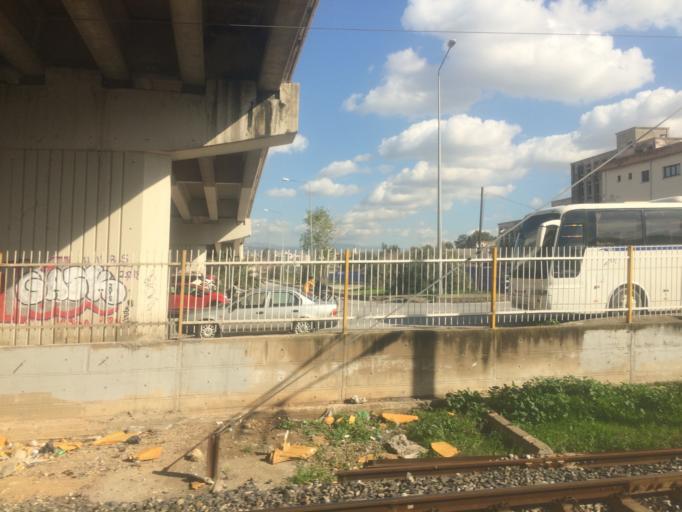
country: TR
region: Izmir
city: Izmir
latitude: 38.4605
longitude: 27.1666
